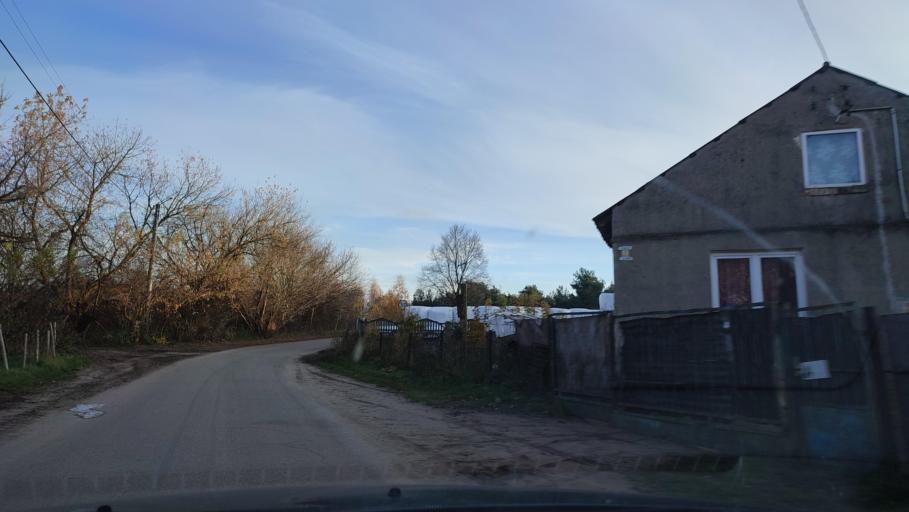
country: PL
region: Masovian Voivodeship
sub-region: Powiat mlawski
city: Dzierzgowo
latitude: 53.2675
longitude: 20.6472
